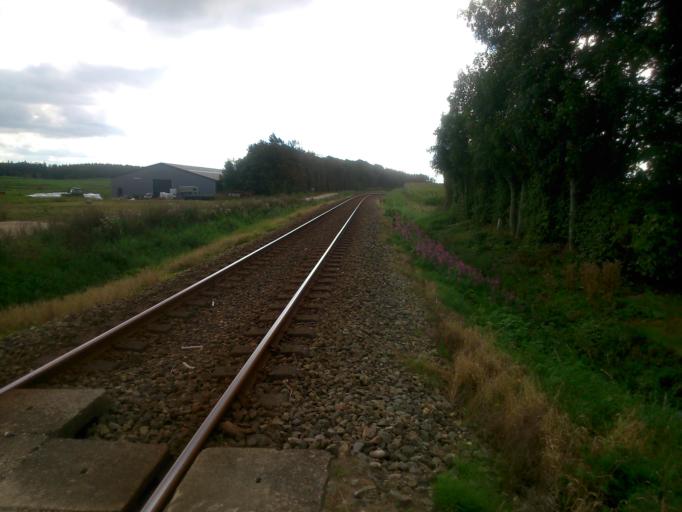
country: DK
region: North Denmark
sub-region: Thisted Kommune
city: Thisted
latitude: 56.9490
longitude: 8.5866
